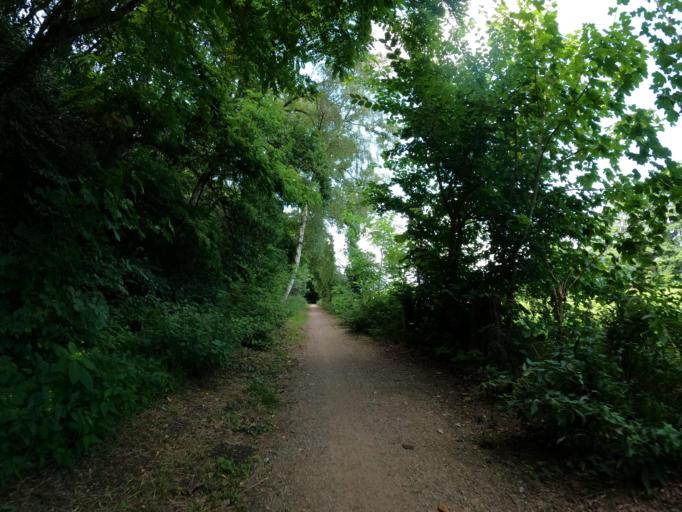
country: DE
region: Mecklenburg-Vorpommern
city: Malchow
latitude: 53.4937
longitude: 12.4376
